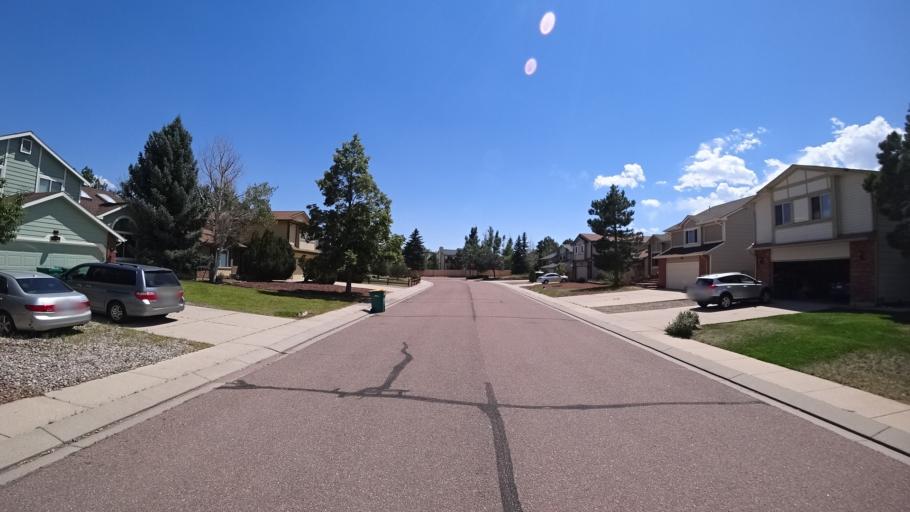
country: US
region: Colorado
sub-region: El Paso County
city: Black Forest
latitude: 38.9503
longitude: -104.7472
